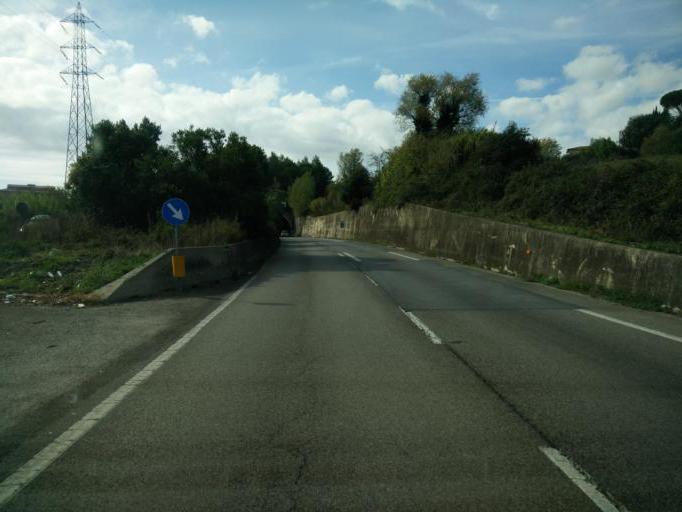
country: IT
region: Tuscany
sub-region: Provincia di Siena
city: Belverde
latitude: 43.3426
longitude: 11.2960
